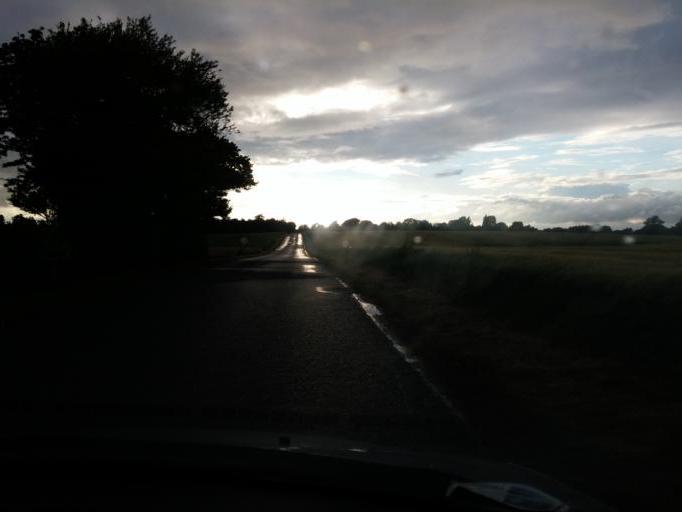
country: DK
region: South Denmark
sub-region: Kerteminde Kommune
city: Kerteminde
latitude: 55.5081
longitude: 10.6260
